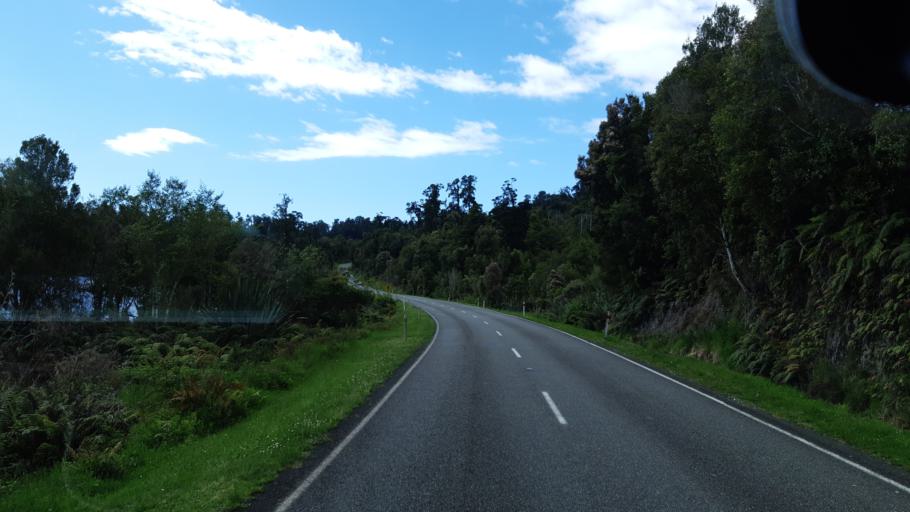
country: NZ
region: West Coast
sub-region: Westland District
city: Hokitika
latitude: -43.0519
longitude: 170.6377
